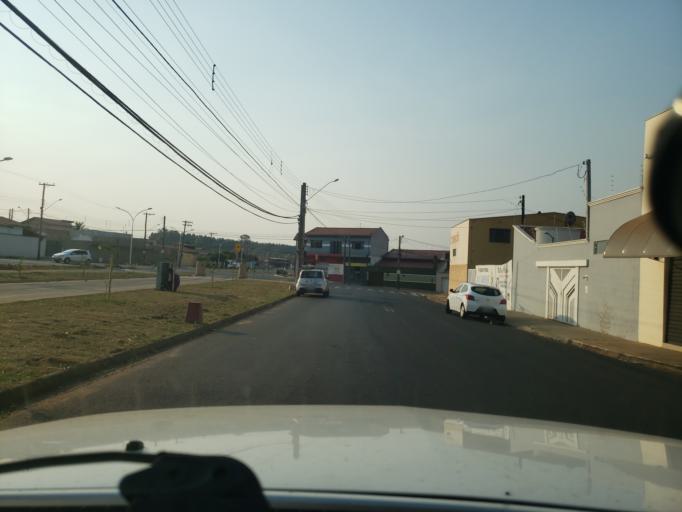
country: BR
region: Sao Paulo
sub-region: Moji-Guacu
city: Mogi-Gaucu
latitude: -22.3318
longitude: -46.9477
